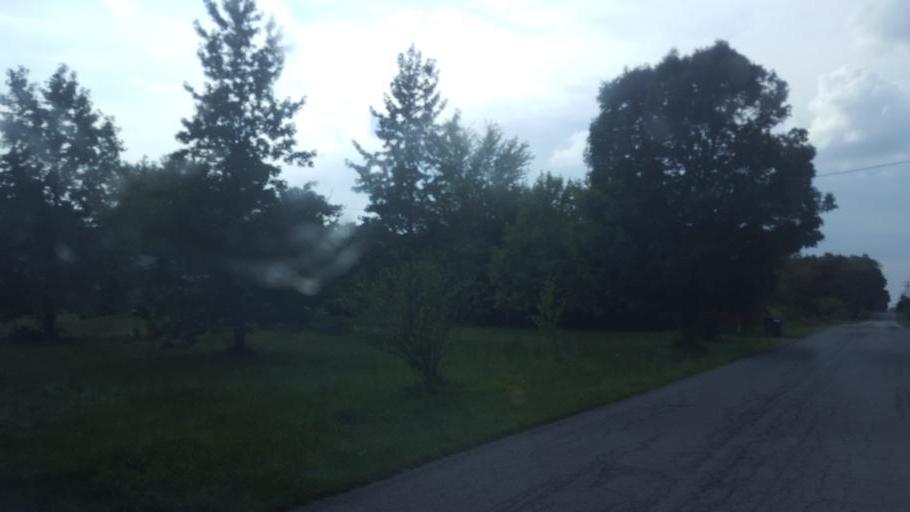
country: US
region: Ohio
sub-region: Knox County
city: Fredericktown
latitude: 40.4321
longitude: -82.6514
